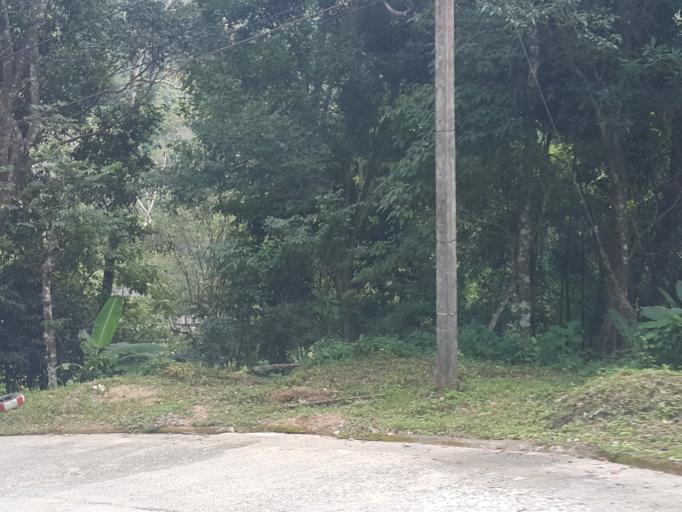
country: TH
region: Chiang Mai
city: Mae On
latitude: 18.8844
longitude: 99.3575
